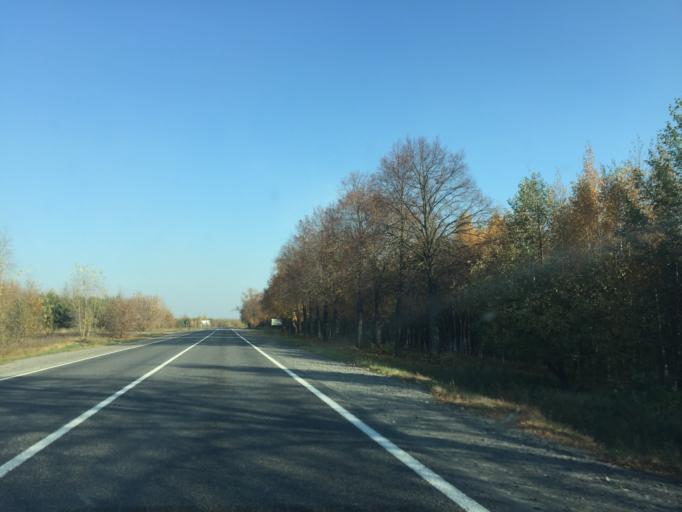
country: BY
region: Gomel
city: Dobrush
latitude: 52.3881
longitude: 31.4512
